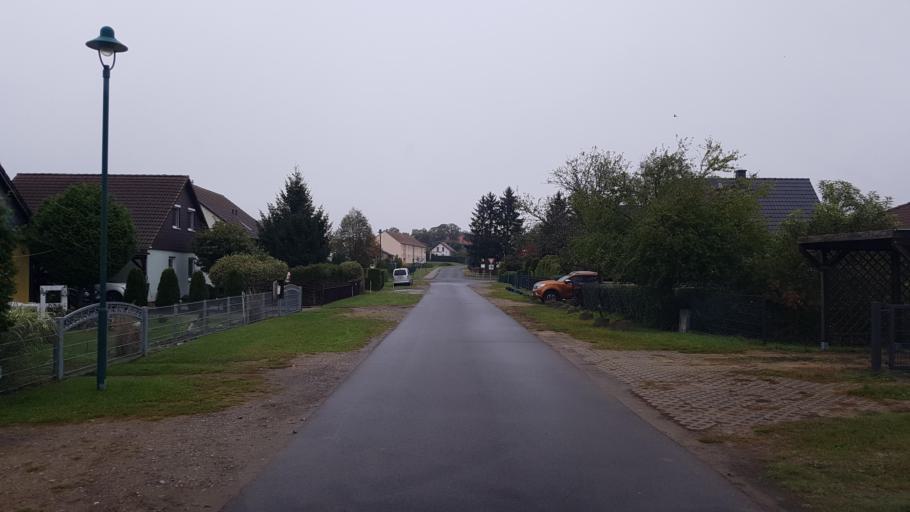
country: DE
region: Brandenburg
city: Furstenwalde
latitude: 52.4303
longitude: 14.0184
